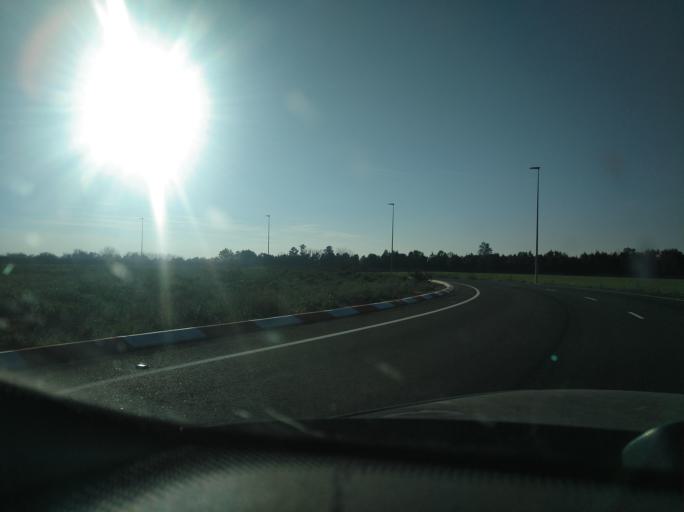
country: ES
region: Extremadura
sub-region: Provincia de Badajoz
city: Badajoz
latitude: 38.8749
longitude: -7.0307
